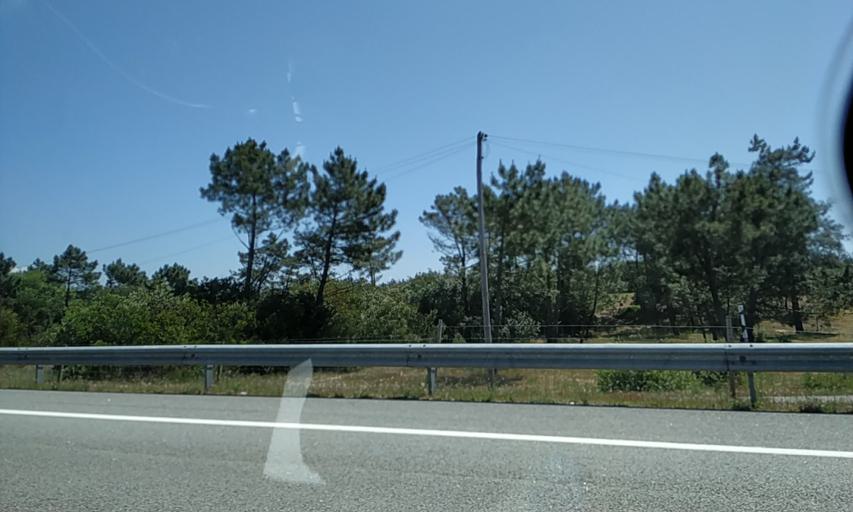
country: PT
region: Aveiro
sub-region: Ilhavo
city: Gafanha da Nazare
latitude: 40.6285
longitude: -8.7035
